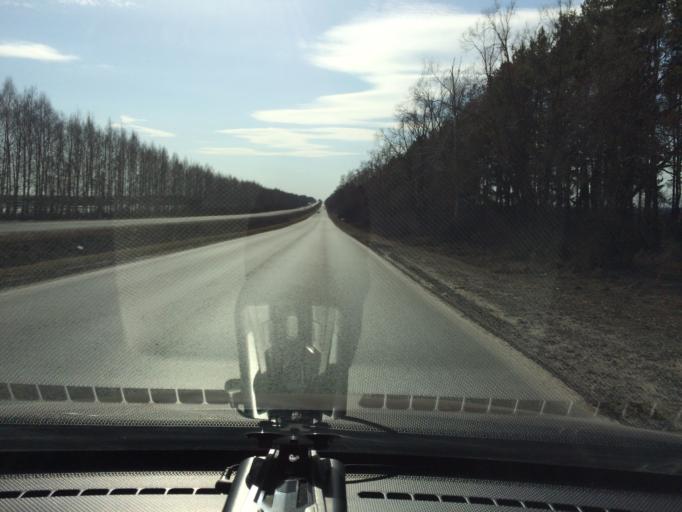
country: RU
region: Mariy-El
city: Yoshkar-Ola
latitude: 56.7358
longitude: 48.1661
